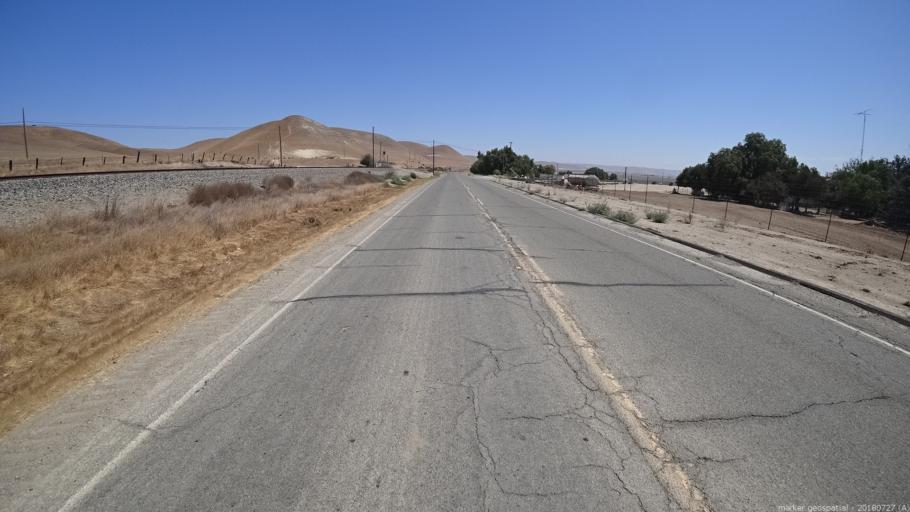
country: US
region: California
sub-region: Monterey County
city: King City
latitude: 36.1045
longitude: -120.9835
